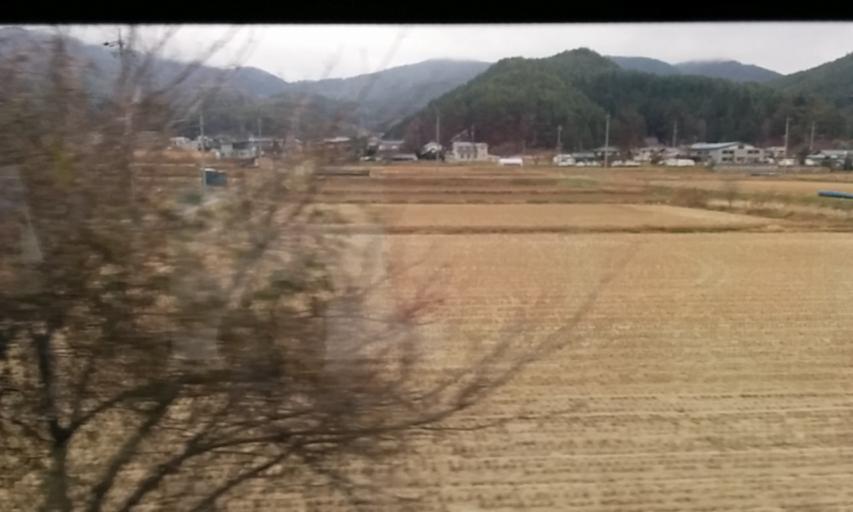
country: JP
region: Nagano
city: Omachi
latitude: 36.4558
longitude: 138.0545
